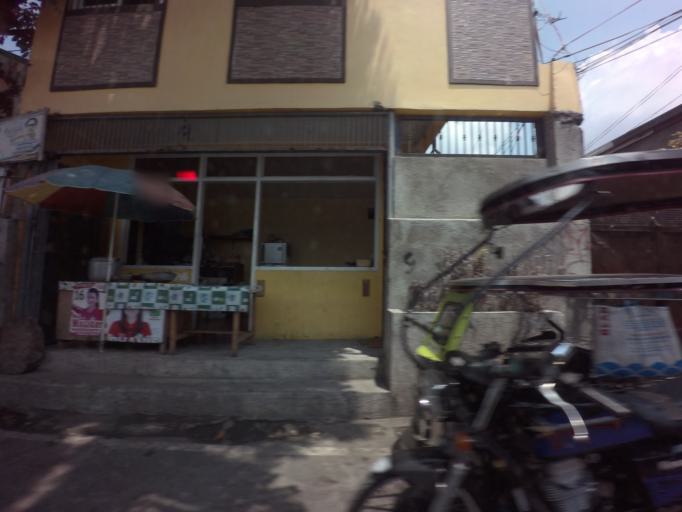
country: PH
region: Calabarzon
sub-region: Province of Laguna
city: San Pedro
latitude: 14.4092
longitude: 121.0500
